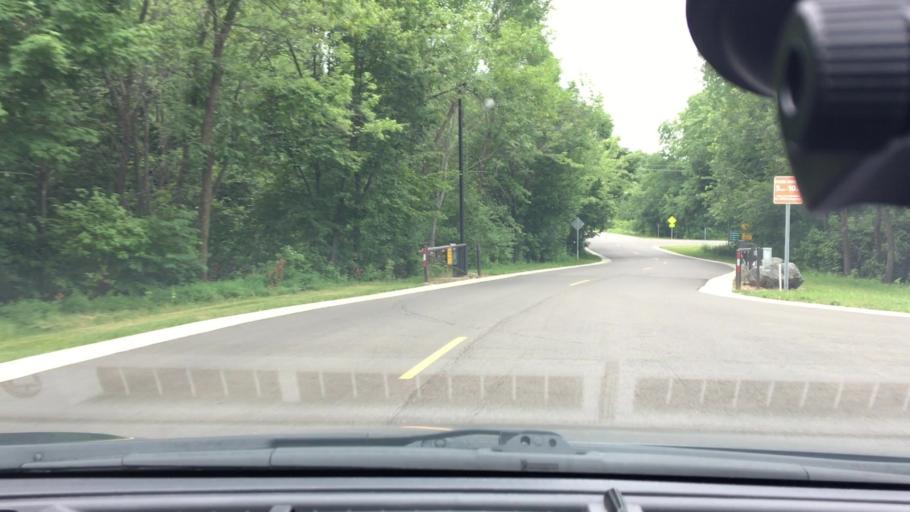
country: US
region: Minnesota
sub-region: Hennepin County
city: Plymouth
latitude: 45.0299
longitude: -93.4385
